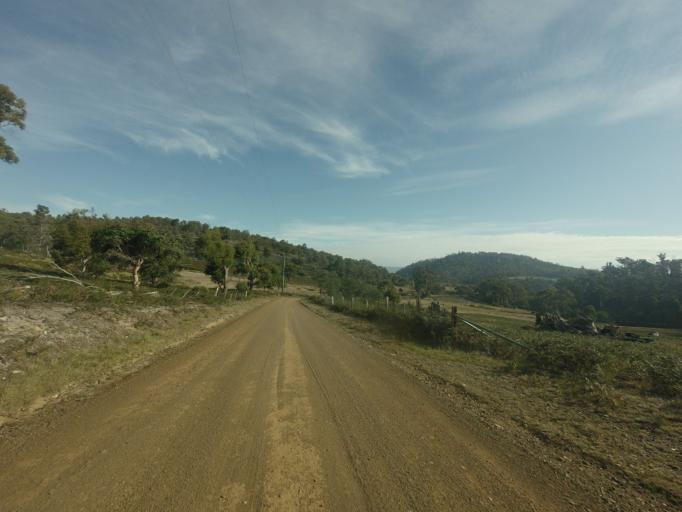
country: AU
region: Tasmania
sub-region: Sorell
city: Sorell
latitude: -42.5304
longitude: 147.4436
